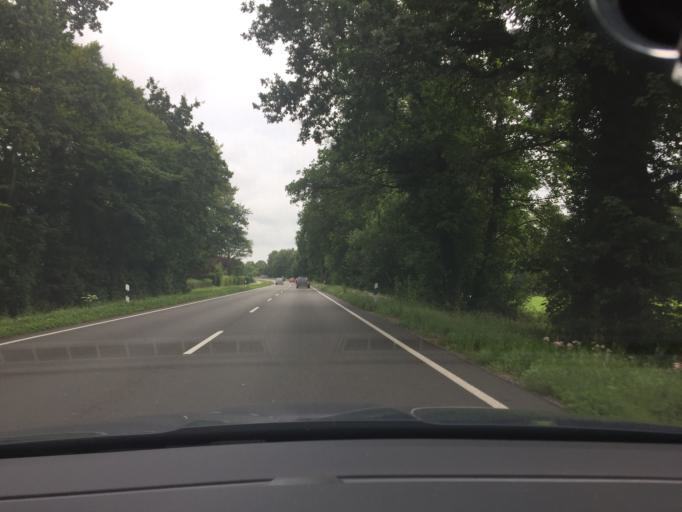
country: DE
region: Lower Saxony
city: Aurich
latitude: 53.4498
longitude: 7.5047
